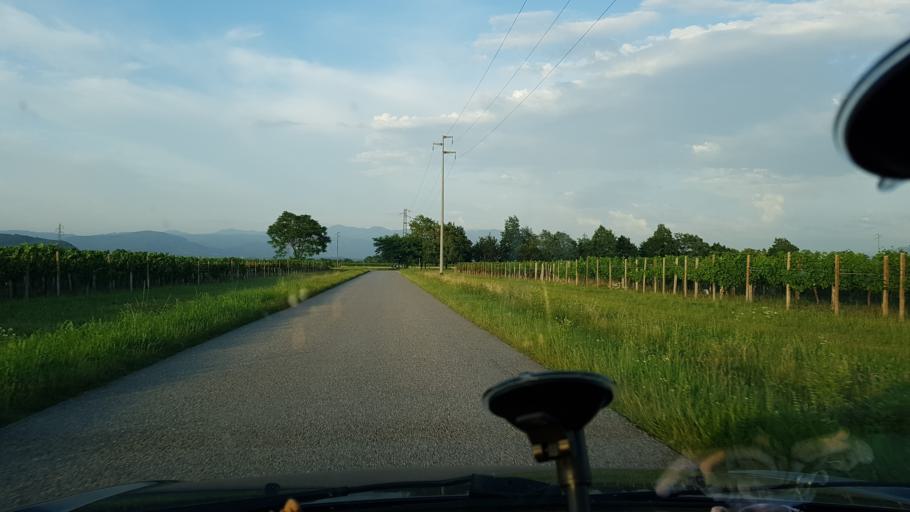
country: IT
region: Friuli Venezia Giulia
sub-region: Provincia di Gorizia
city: Mossa
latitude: 45.9151
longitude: 13.5434
